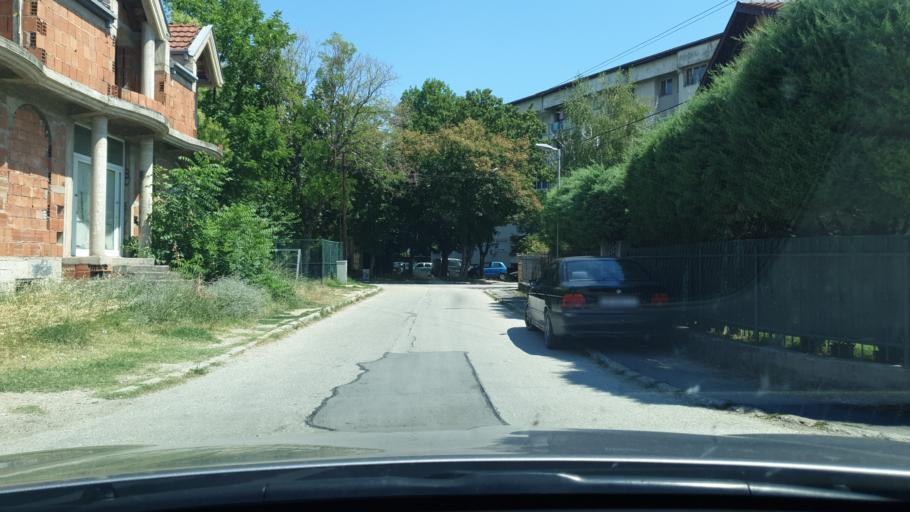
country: MK
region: Kisela Voda
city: Kisela Voda
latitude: 41.9427
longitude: 21.5177
